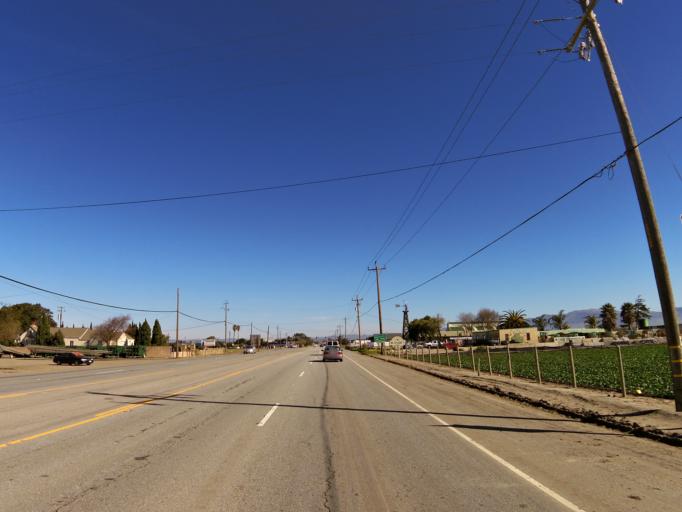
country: US
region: California
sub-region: Monterey County
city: Salinas
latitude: 36.6417
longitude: -121.6653
